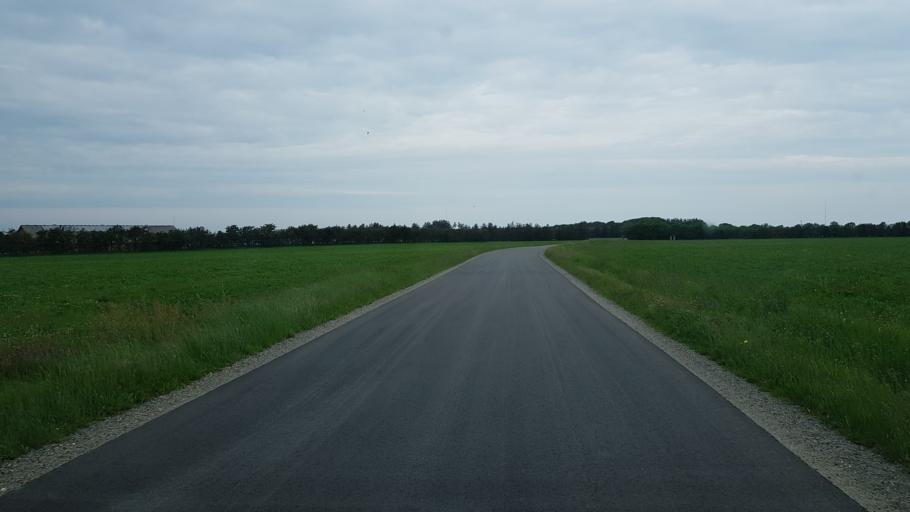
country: DK
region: South Denmark
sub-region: Varde Kommune
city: Oksbol
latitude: 55.7445
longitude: 8.3737
